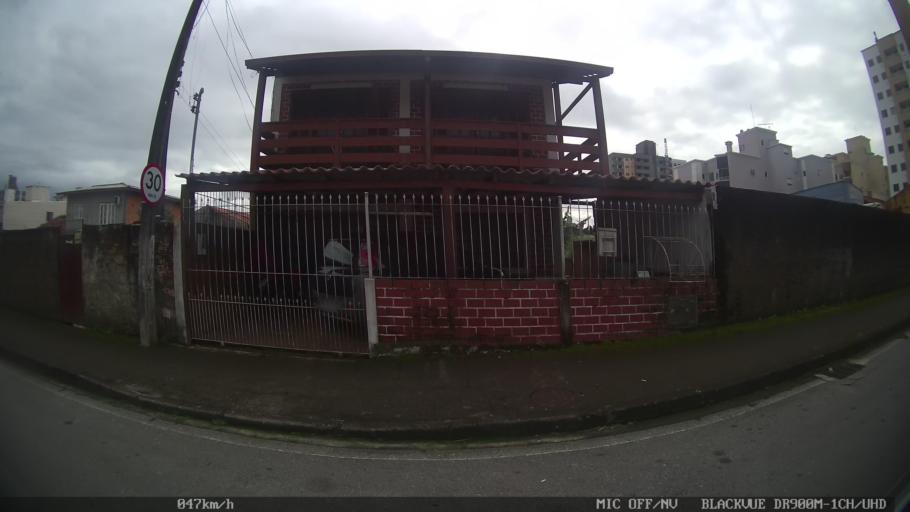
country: BR
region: Santa Catarina
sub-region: Sao Jose
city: Campinas
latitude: -27.5658
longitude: -48.6207
